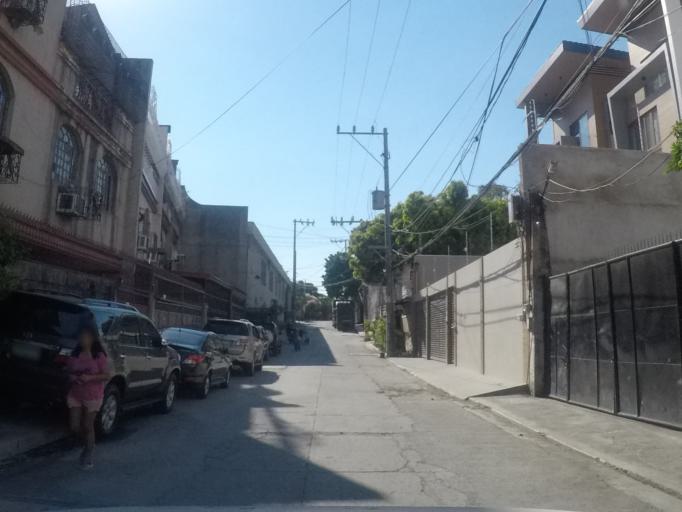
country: PH
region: Metro Manila
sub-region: San Juan
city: San Juan
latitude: 14.6065
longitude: 121.0335
